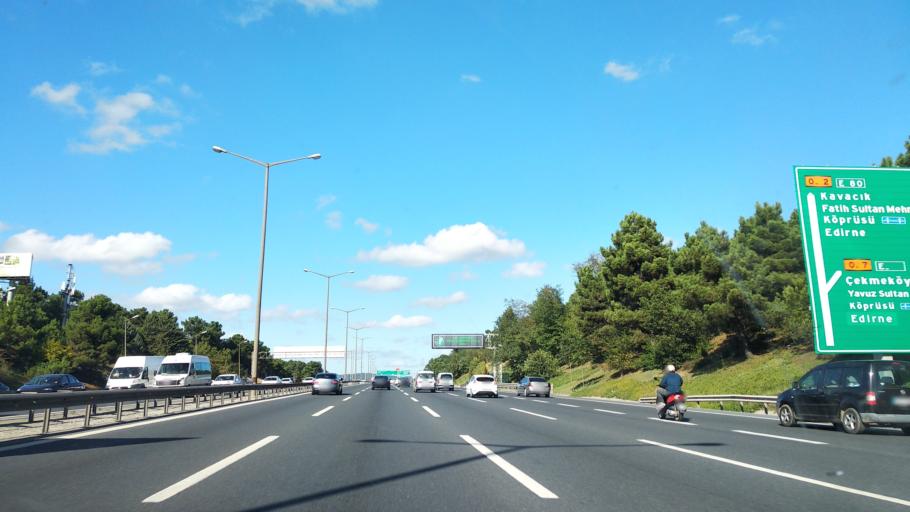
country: TR
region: Istanbul
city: Umraniye
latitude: 41.0364
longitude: 29.1212
